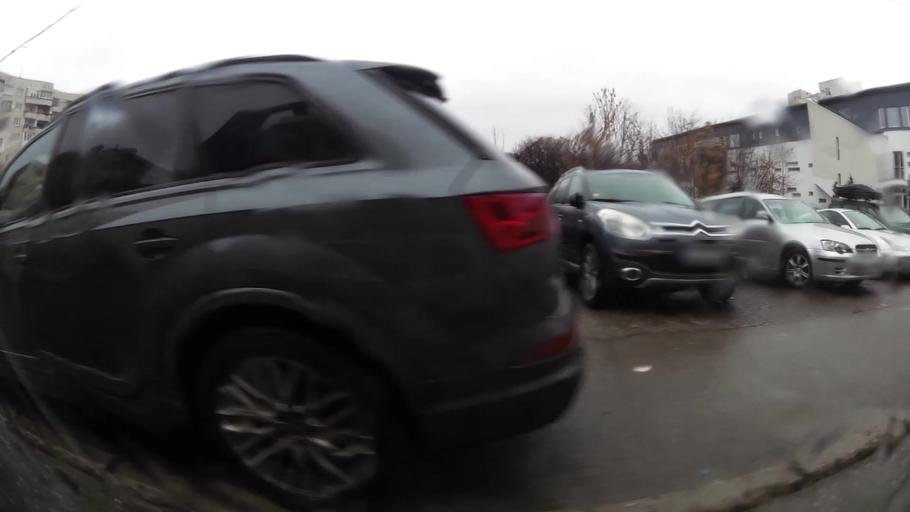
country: BG
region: Sofia-Capital
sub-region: Stolichna Obshtina
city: Sofia
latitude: 42.6636
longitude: 23.3633
